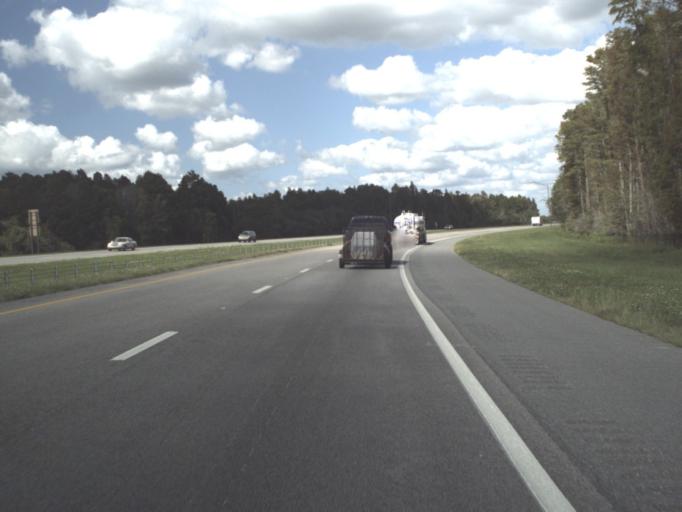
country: US
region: Florida
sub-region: Pasco County
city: Shady Hills
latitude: 28.3203
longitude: -82.5529
